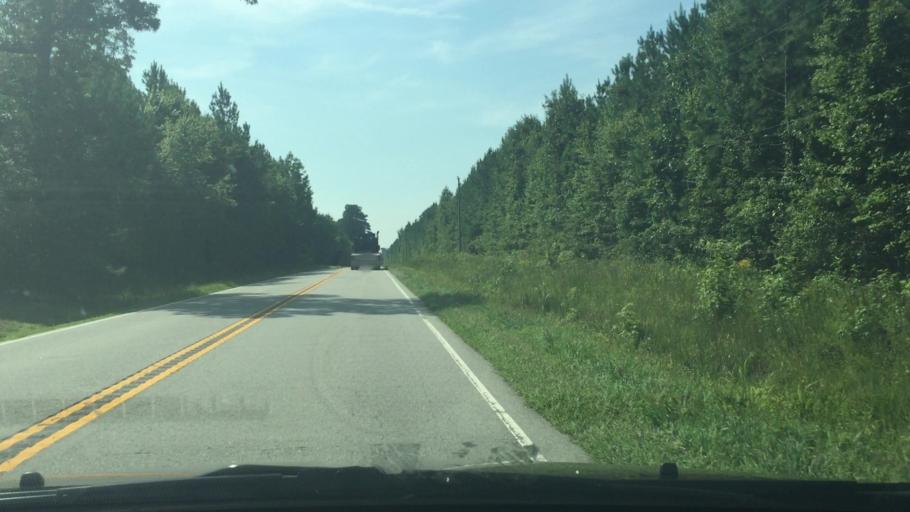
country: US
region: Virginia
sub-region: Sussex County
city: Sussex
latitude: 36.8679
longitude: -77.1415
